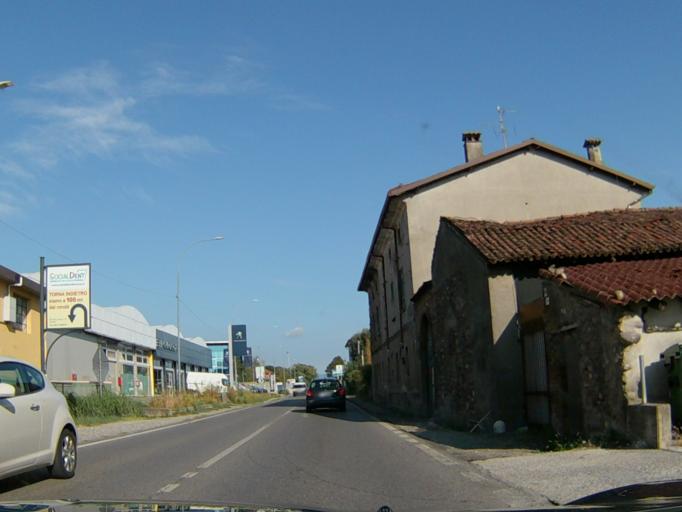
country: IT
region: Lombardy
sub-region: Provincia di Brescia
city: Rovato
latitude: 45.5621
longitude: 9.9892
